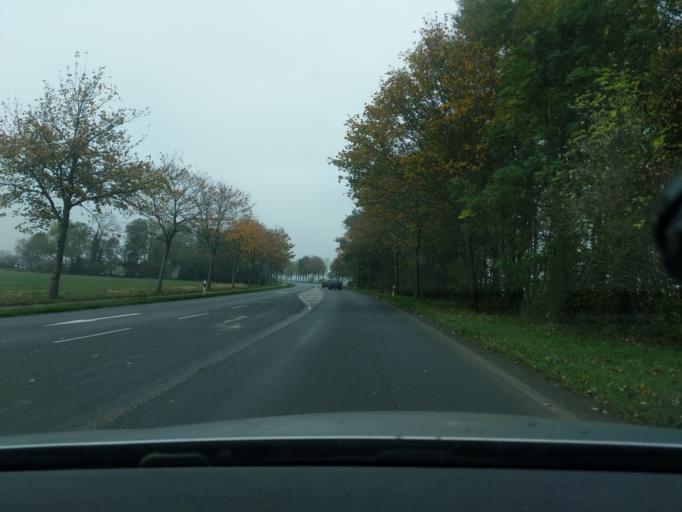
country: DE
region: Lower Saxony
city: Cuxhaven
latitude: 53.8332
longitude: 8.7393
